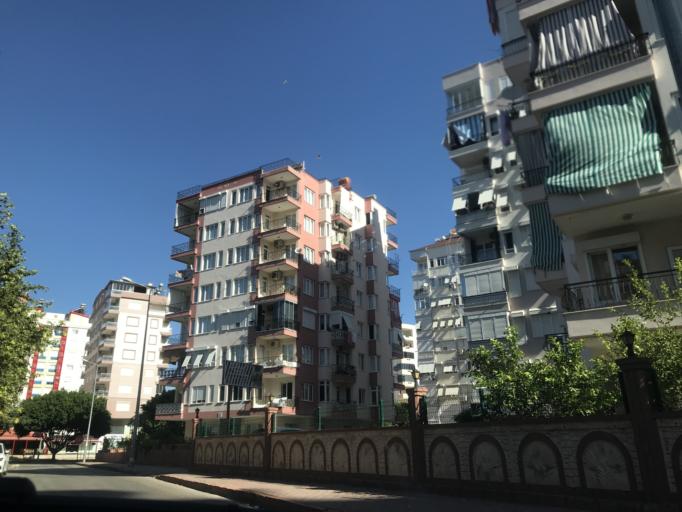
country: TR
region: Antalya
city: Antalya
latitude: 36.8954
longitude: 30.6296
